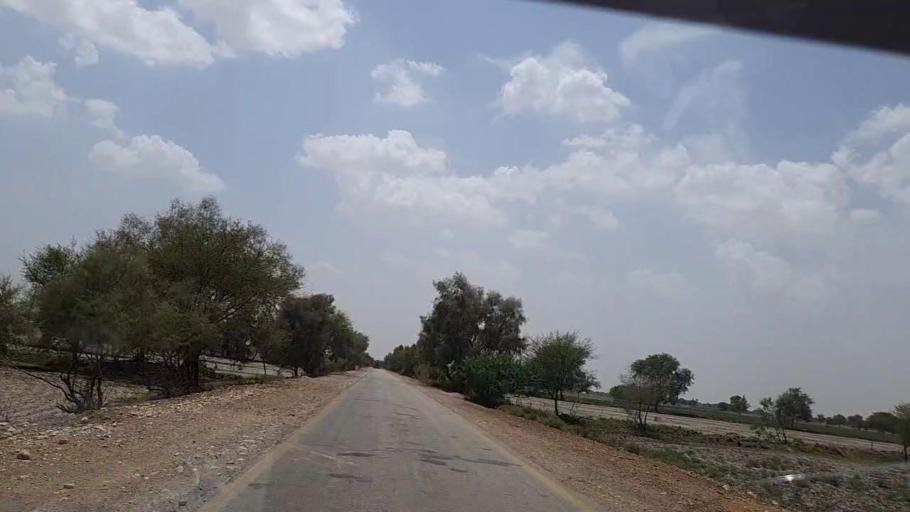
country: PK
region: Sindh
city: Bhan
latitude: 26.5408
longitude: 67.6714
